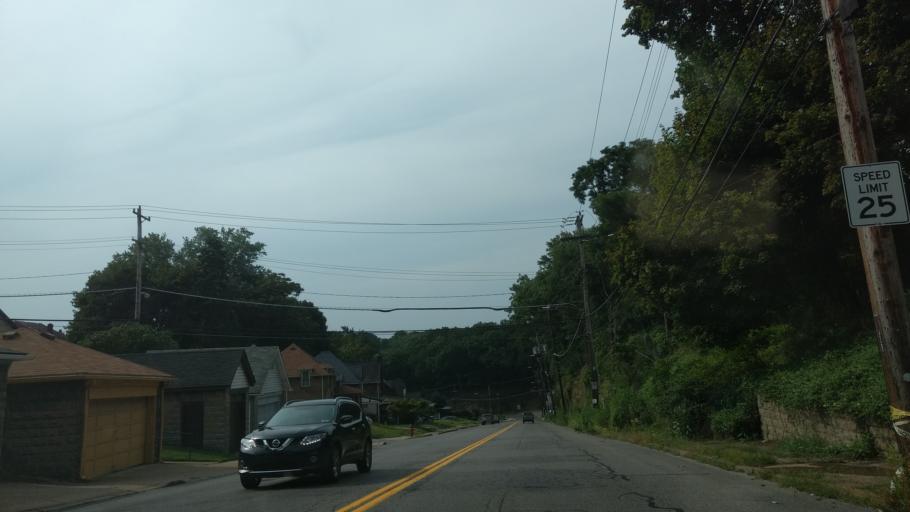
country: US
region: Pennsylvania
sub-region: Allegheny County
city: Bellevue
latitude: 40.4882
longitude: -80.0415
